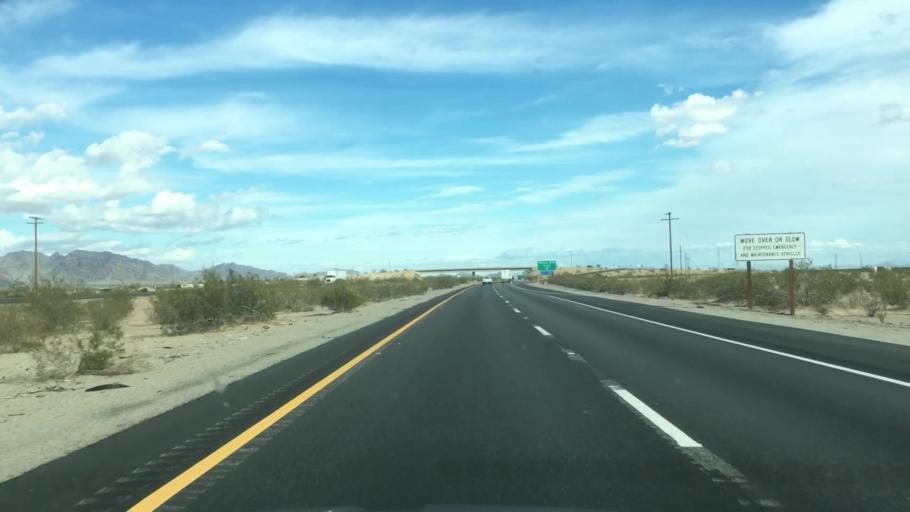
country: US
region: California
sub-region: Riverside County
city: Mesa Verde
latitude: 33.6074
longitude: -114.9077
